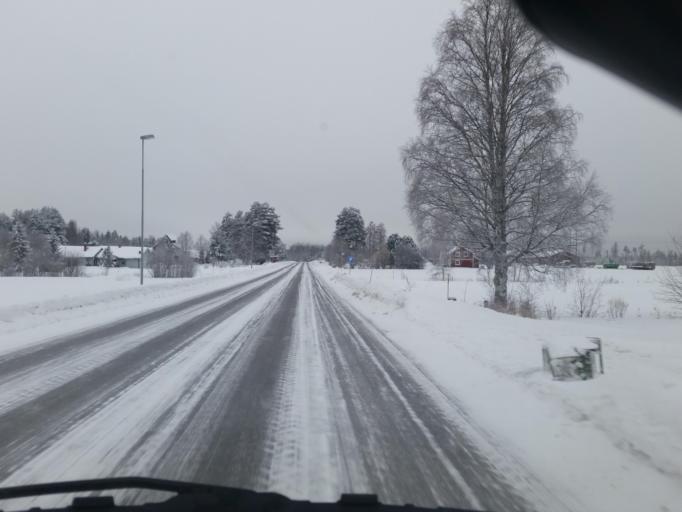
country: SE
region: Norrbotten
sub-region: Pitea Kommun
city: Roknas
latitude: 65.4402
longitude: 21.2686
